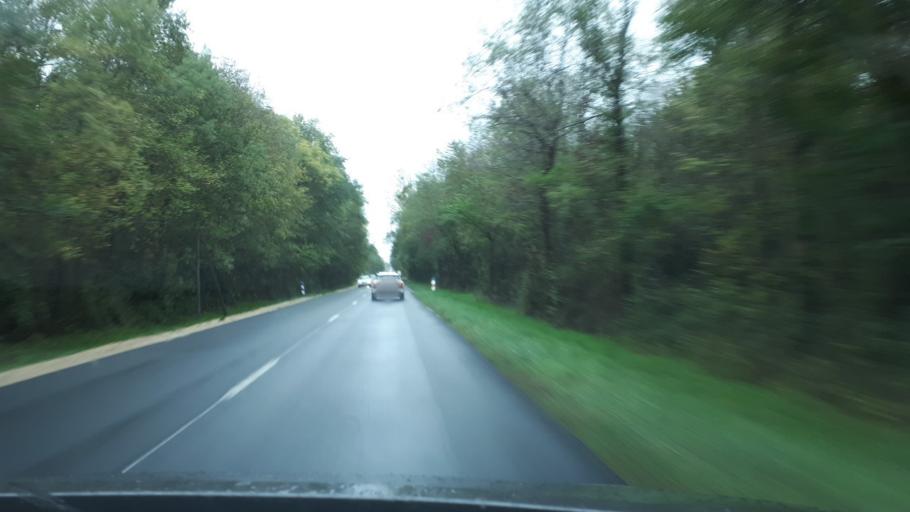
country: FR
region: Centre
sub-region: Departement du Loir-et-Cher
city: Gievres
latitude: 47.2676
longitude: 1.6608
